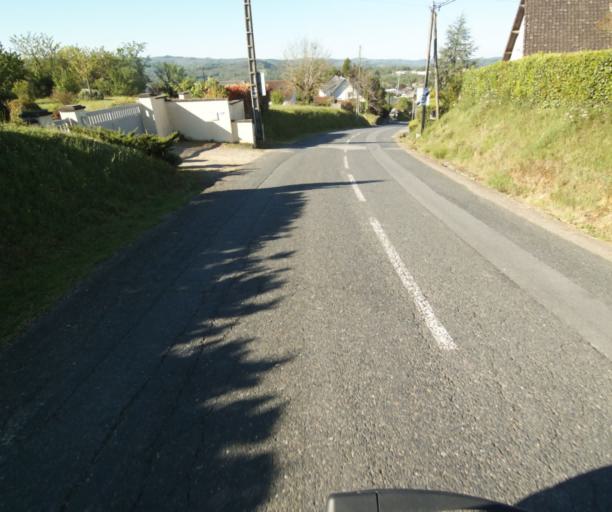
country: FR
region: Limousin
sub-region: Departement de la Correze
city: Tulle
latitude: 45.2670
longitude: 1.7853
